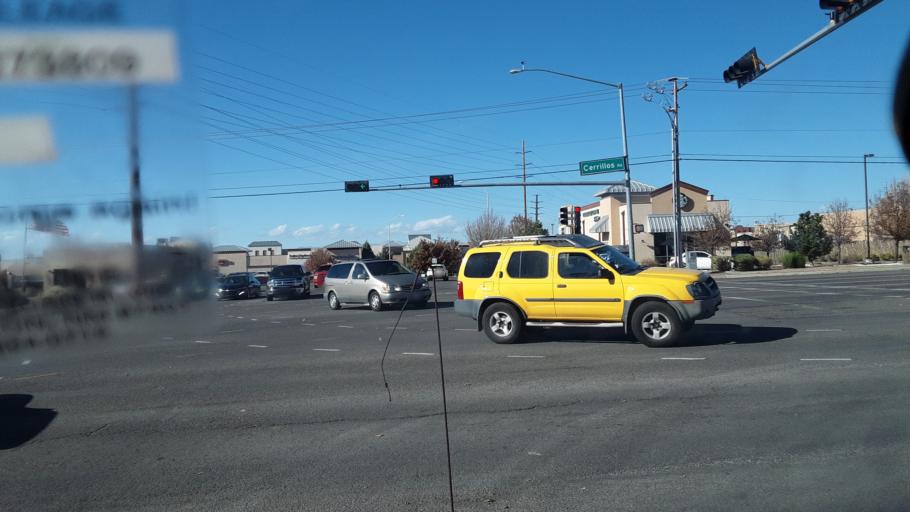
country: US
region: New Mexico
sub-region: Santa Fe County
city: Agua Fria
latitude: 35.6422
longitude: -106.0125
